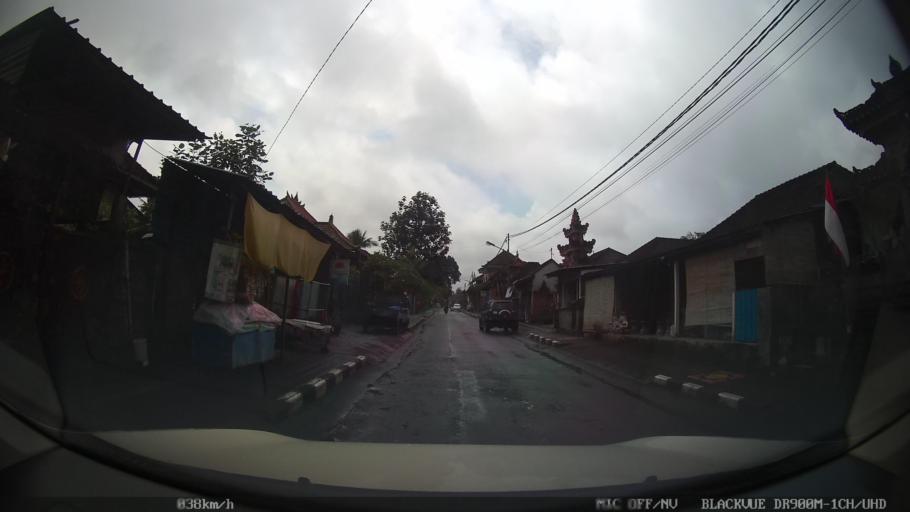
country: ID
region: Bali
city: Pegongan
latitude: -8.4907
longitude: 115.2263
